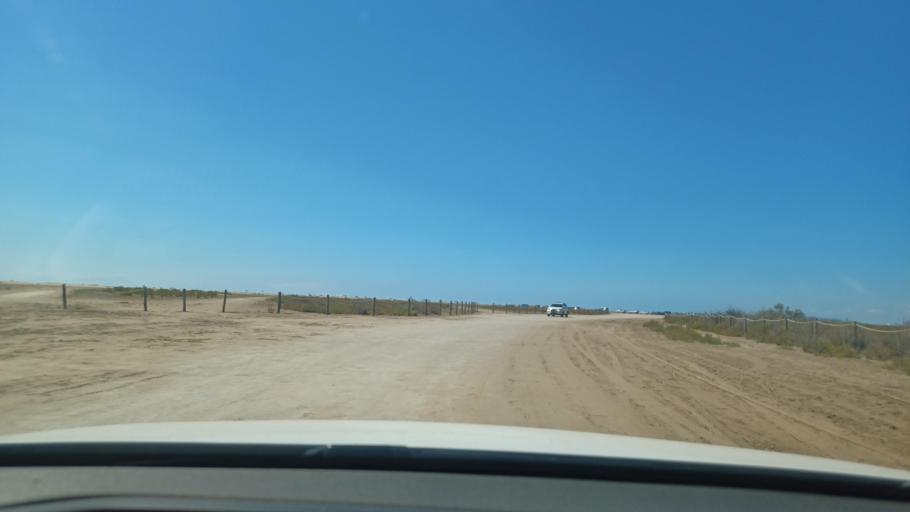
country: ES
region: Catalonia
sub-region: Provincia de Tarragona
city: Deltebre
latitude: 40.6550
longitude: 0.7826
